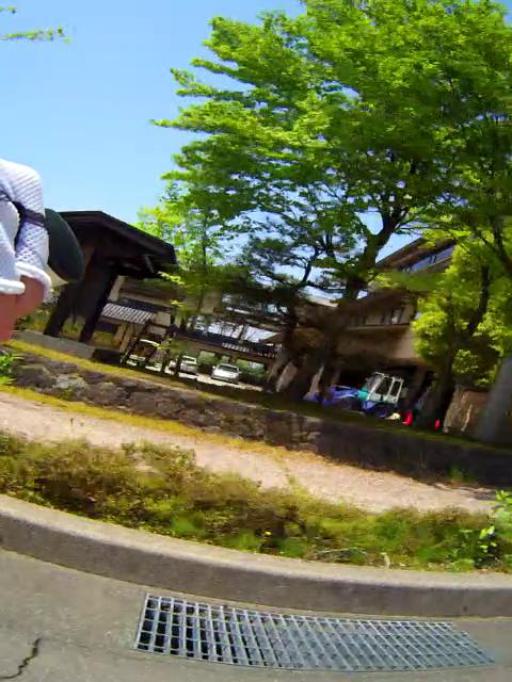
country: JP
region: Ishikawa
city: Tsurugi-asahimachi
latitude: 36.4900
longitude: 136.7562
